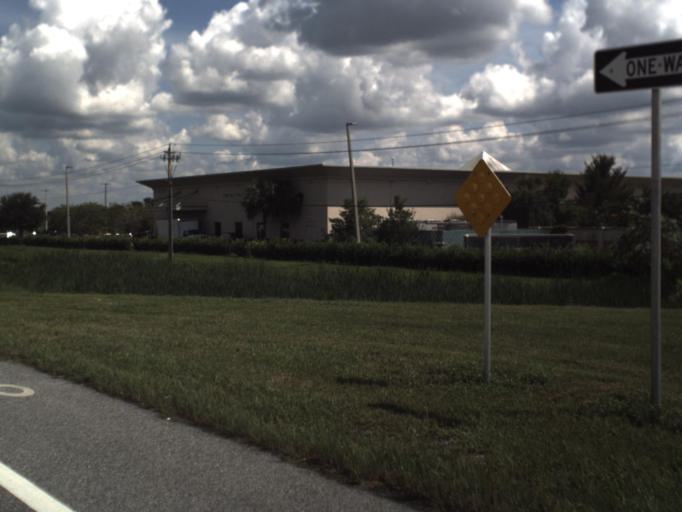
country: US
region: Florida
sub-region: Sarasota County
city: Fruitville
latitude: 27.3385
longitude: -82.4400
